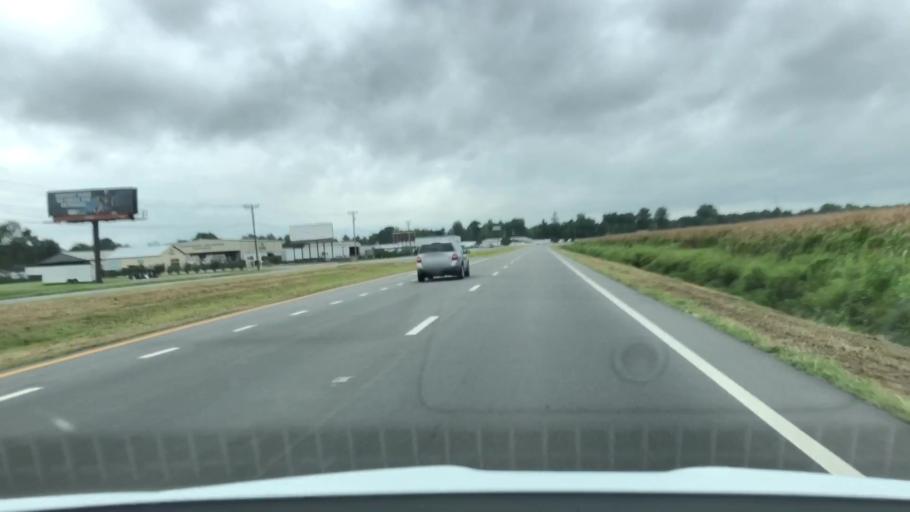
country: US
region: North Carolina
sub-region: Lenoir County
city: La Grange
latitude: 35.2683
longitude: -77.7351
